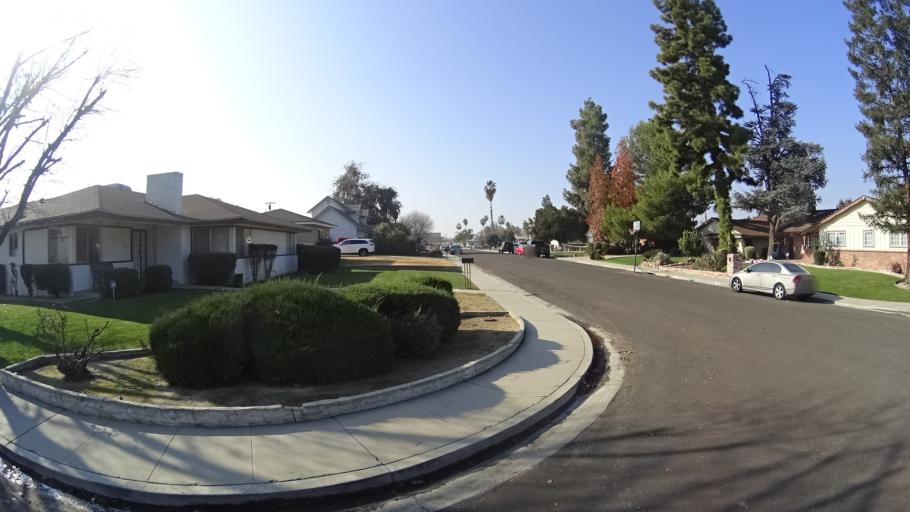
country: US
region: California
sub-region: Kern County
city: Bakersfield
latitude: 35.3412
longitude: -119.0462
